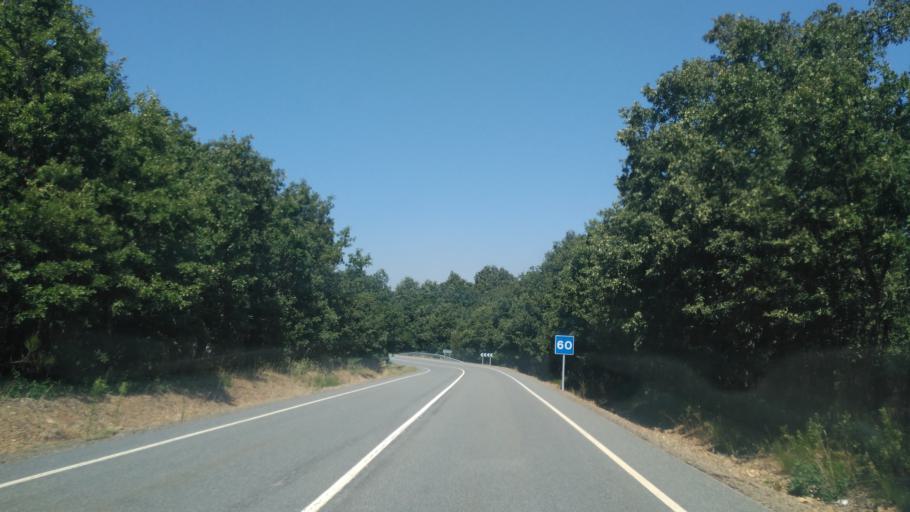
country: ES
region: Castille and Leon
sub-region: Provincia de Salamanca
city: Cilleros de la Bastida
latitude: 40.5673
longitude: -6.0733
